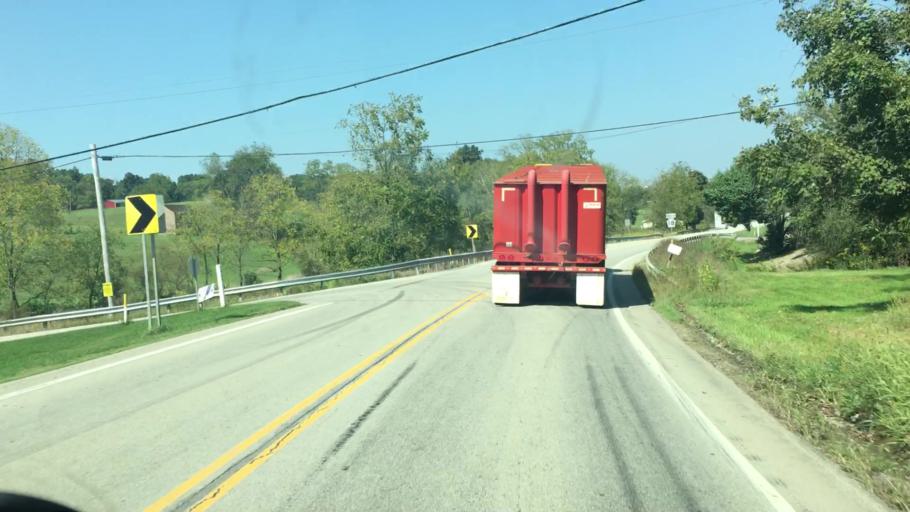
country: US
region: Pennsylvania
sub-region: Washington County
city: Washington
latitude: 40.1047
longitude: -80.2928
